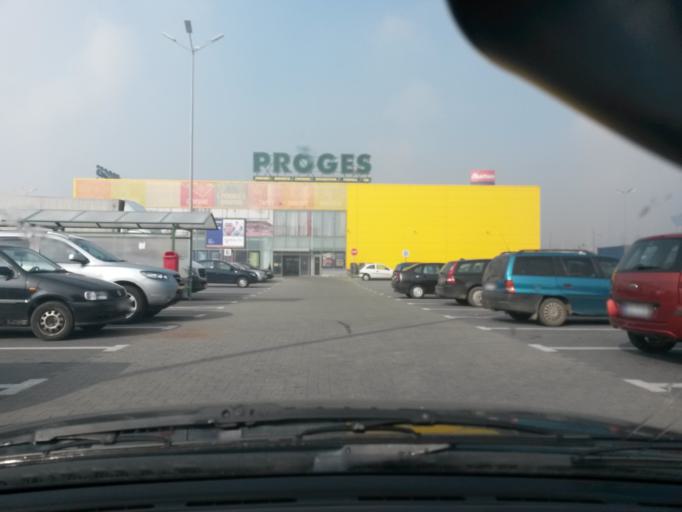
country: RO
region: Mures
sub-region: Comuna Sancraiu de Mures
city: Nazna
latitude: 46.5106
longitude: 24.5123
